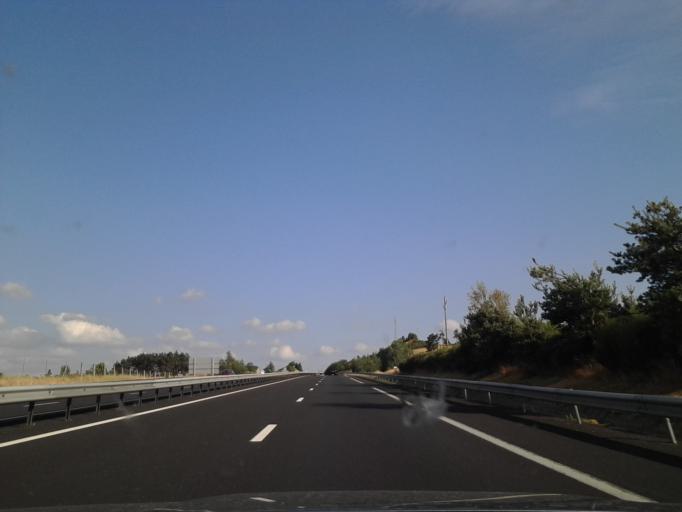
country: FR
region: Languedoc-Roussillon
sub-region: Departement de la Lozere
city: Le Malzieu-Ville
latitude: 44.9277
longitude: 3.2067
